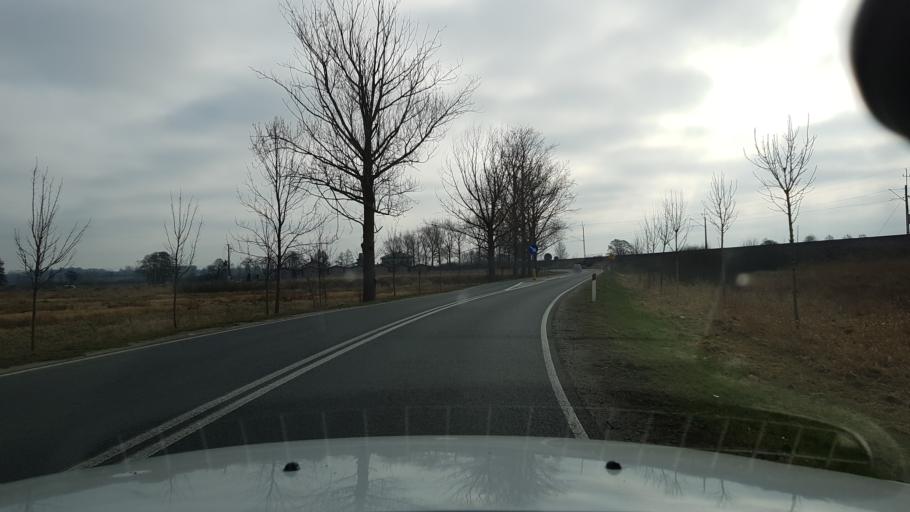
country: PL
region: West Pomeranian Voivodeship
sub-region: Powiat koszalinski
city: Sianow
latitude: 54.2322
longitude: 16.2600
